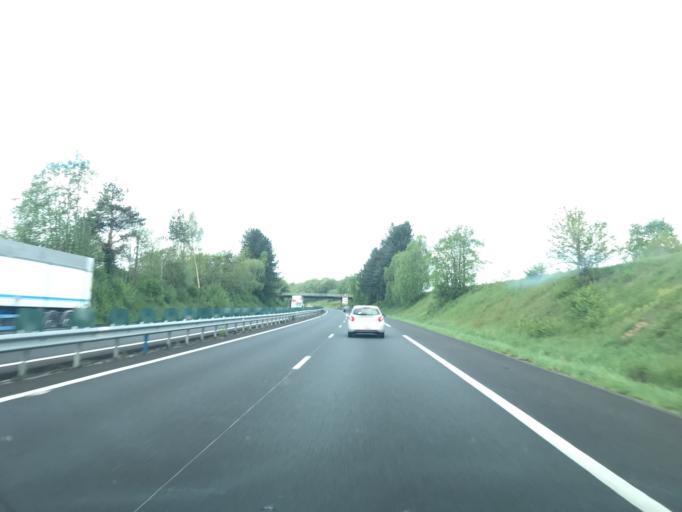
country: FR
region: Haute-Normandie
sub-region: Departement de l'Eure
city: Pont-Audemer
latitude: 49.3941
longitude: 0.5227
